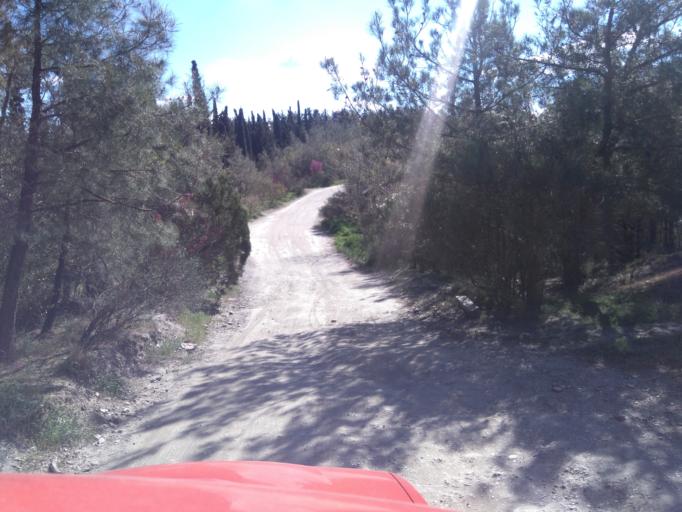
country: GR
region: Central Macedonia
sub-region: Nomos Thessalonikis
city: Agios Pavlos
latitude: 40.6421
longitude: 22.9808
